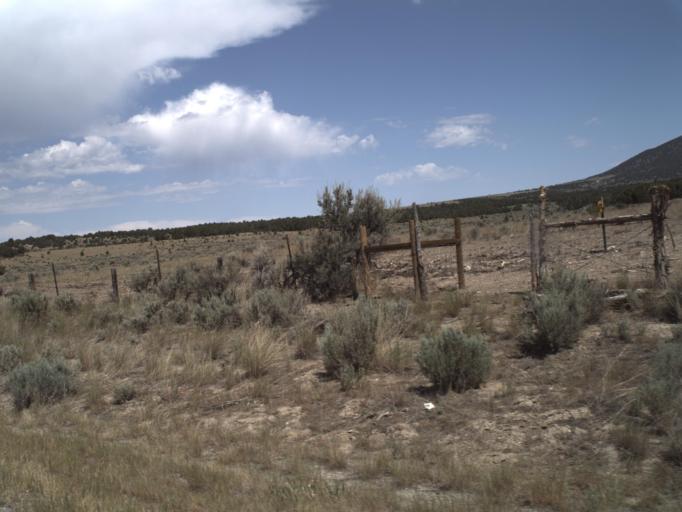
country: US
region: Utah
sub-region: Utah County
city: Genola
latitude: 39.9438
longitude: -112.1990
